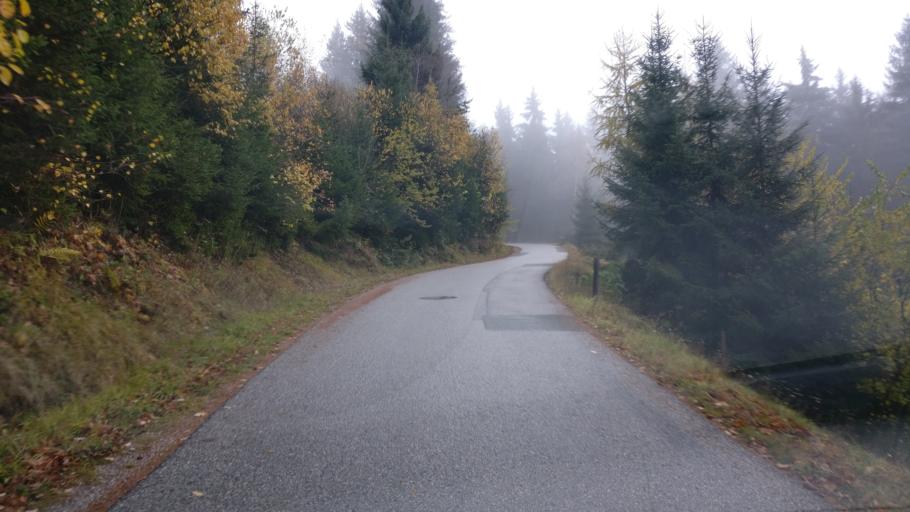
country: AT
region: Salzburg
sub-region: Politischer Bezirk Sankt Johann im Pongau
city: Filzmoos
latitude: 47.4020
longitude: 13.5261
